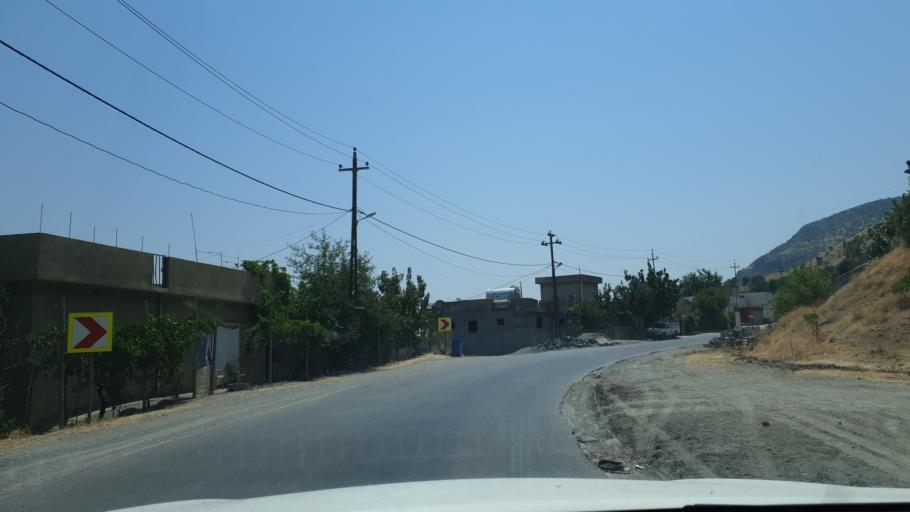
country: IQ
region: Arbil
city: Nahiyat Hiran
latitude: 36.2887
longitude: 44.4848
